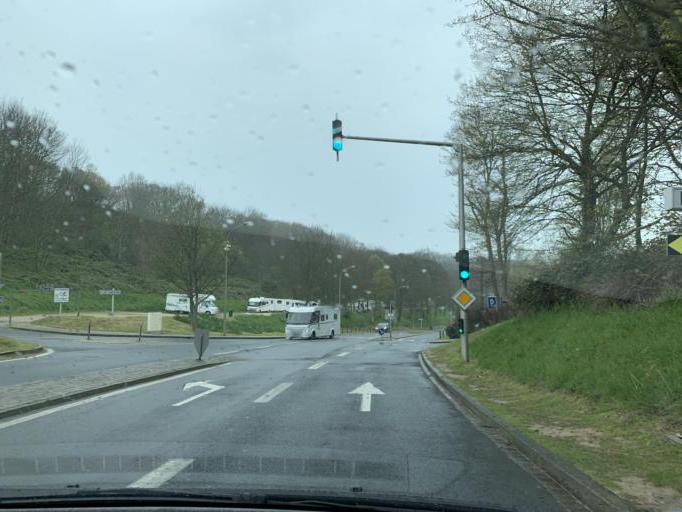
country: FR
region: Haute-Normandie
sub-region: Departement de la Seine-Maritime
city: Etretat
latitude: 49.7008
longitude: 0.2001
